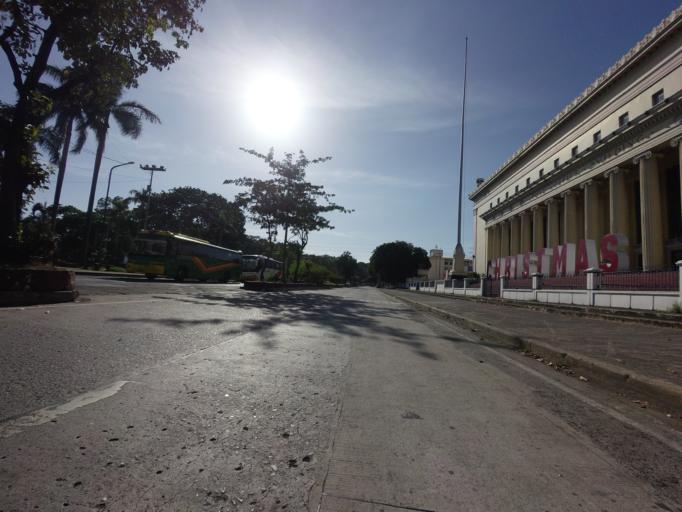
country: PH
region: Metro Manila
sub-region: City of Manila
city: Quiapo
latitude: 14.5952
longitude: 120.9795
